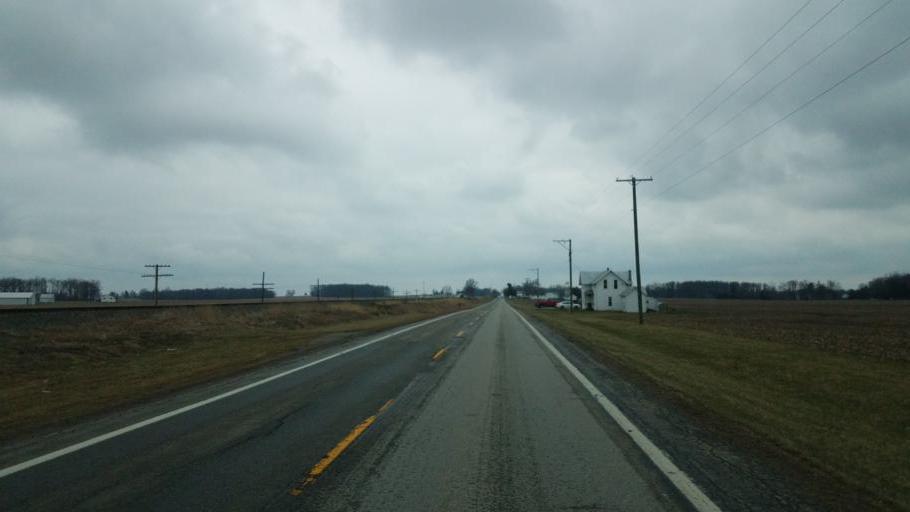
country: US
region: Ohio
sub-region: Delaware County
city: Ashley
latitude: 40.3740
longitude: -82.9784
